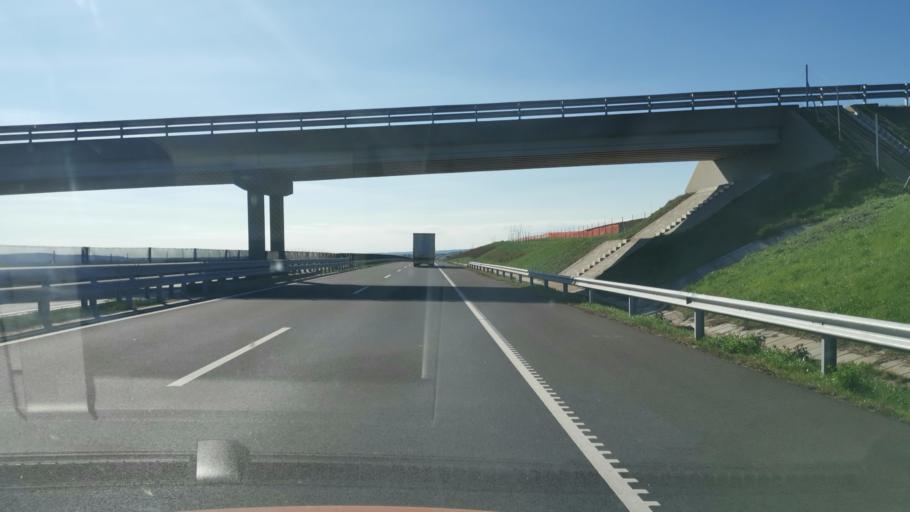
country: HU
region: Borsod-Abauj-Zemplen
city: Halmaj
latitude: 48.2789
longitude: 21.0071
